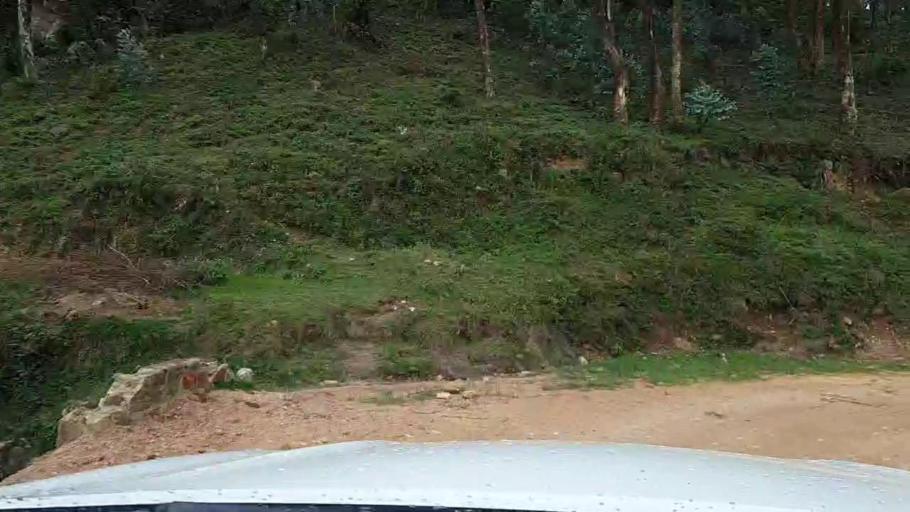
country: RW
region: Western Province
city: Kibuye
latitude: -2.2926
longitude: 29.3816
